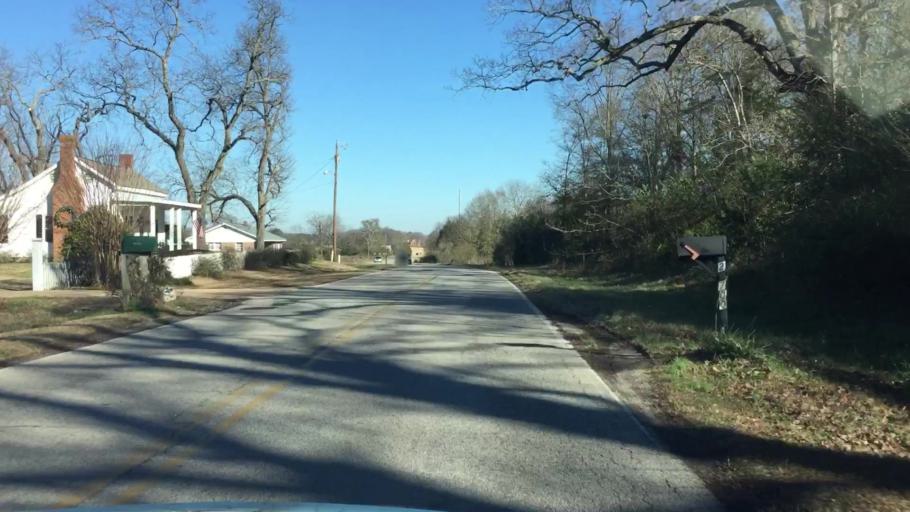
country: US
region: Georgia
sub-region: Newton County
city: Oakwood
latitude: 33.5000
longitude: -84.0562
